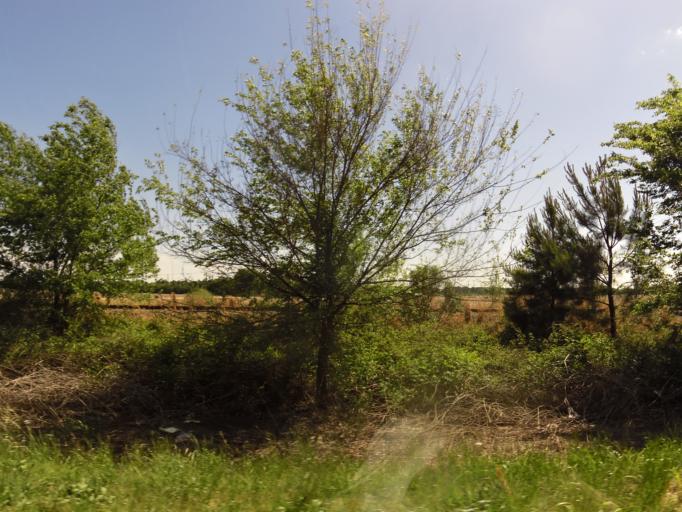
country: US
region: South Carolina
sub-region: Aiken County
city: Aiken
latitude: 33.5390
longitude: -81.6586
